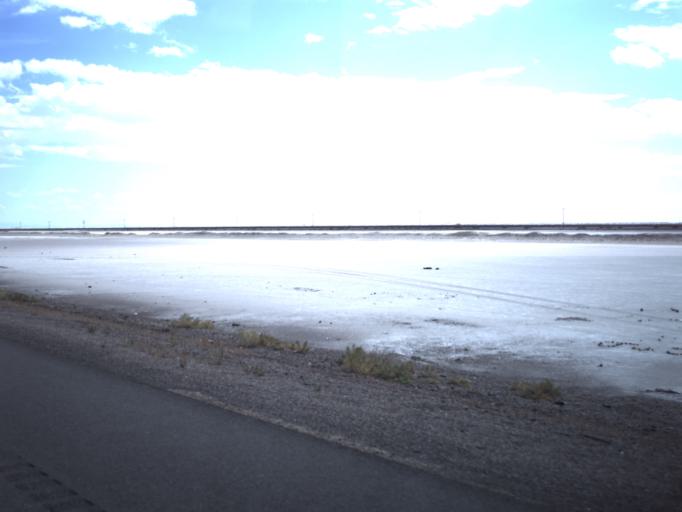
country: US
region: Utah
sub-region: Tooele County
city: Wendover
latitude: 40.7400
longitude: -113.9309
